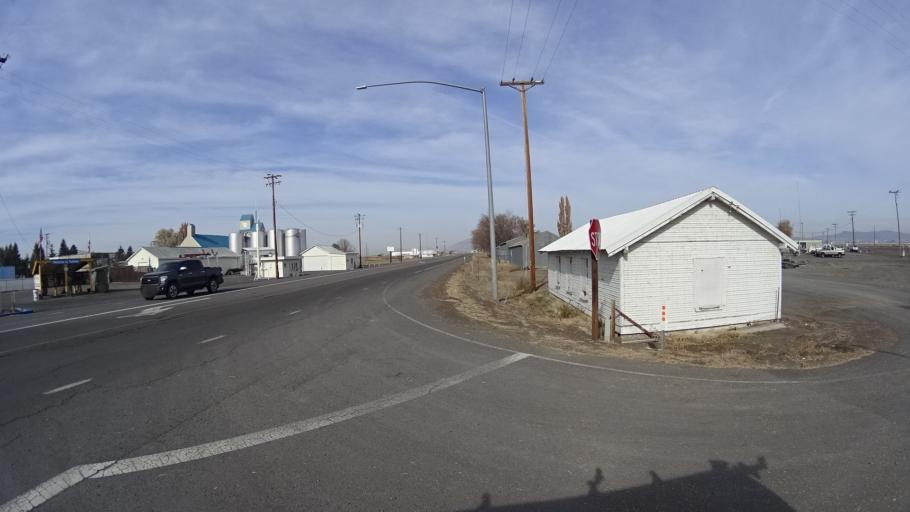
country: US
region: California
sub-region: Siskiyou County
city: Tulelake
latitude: 41.9585
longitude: -121.4748
